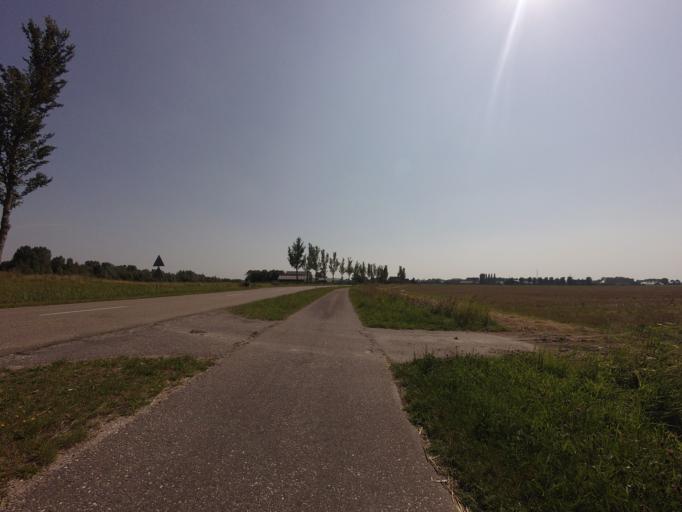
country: NL
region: Groningen
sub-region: Gemeente Zuidhorn
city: Grijpskerk
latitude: 53.2740
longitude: 6.3049
